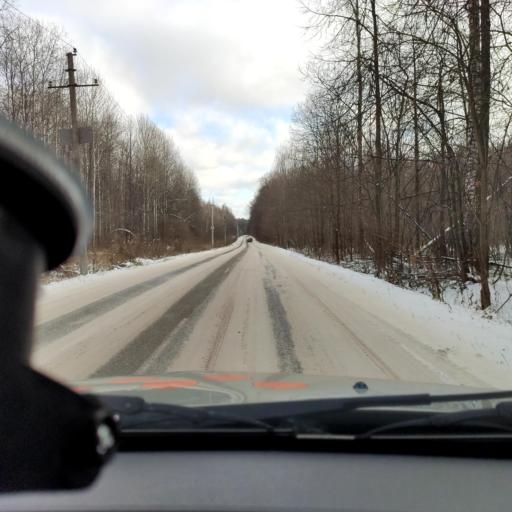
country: RU
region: Bashkortostan
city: Avdon
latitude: 54.7830
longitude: 55.7382
